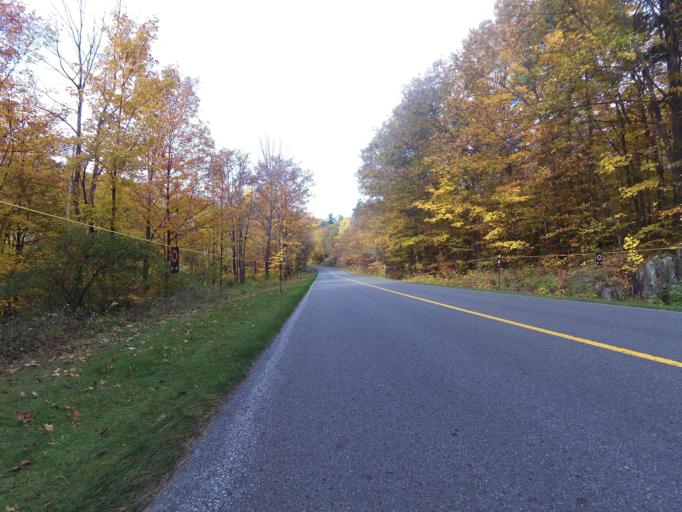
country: CA
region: Quebec
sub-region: Outaouais
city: Gatineau
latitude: 45.4851
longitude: -75.8578
